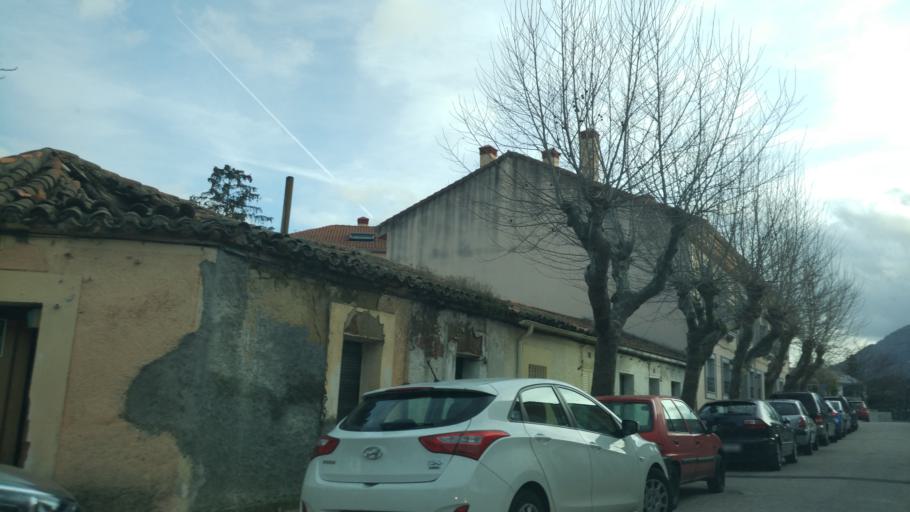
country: ES
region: Madrid
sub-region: Provincia de Madrid
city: El Escorial
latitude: 40.5819
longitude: -4.1308
